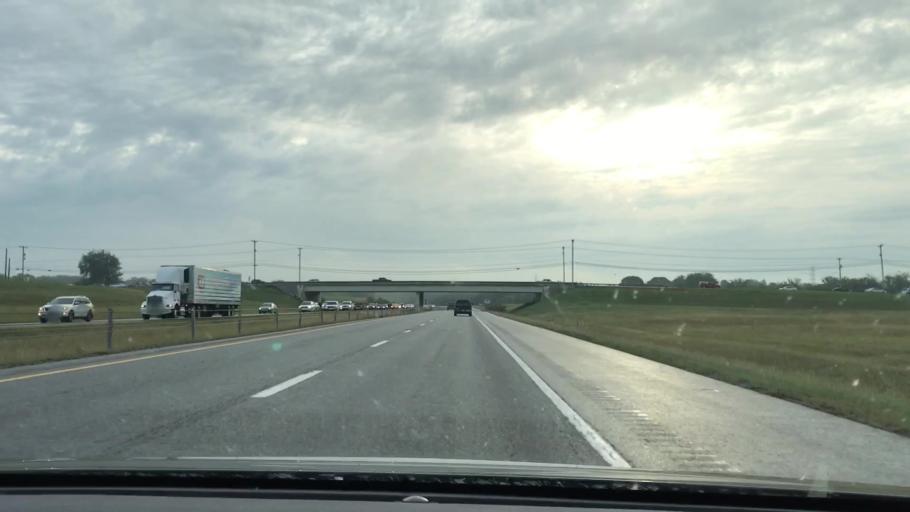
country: US
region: Tennessee
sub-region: Sumner County
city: Hendersonville
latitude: 36.3302
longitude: -86.6214
